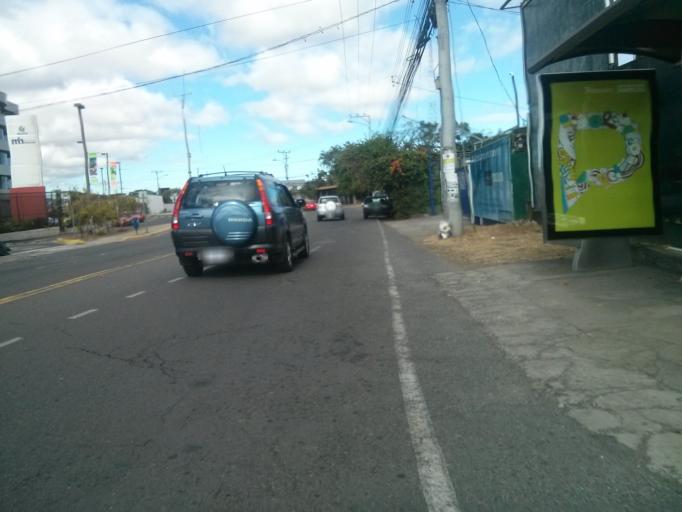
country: CR
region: San Jose
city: San Pedro
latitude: 9.9251
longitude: -84.0570
